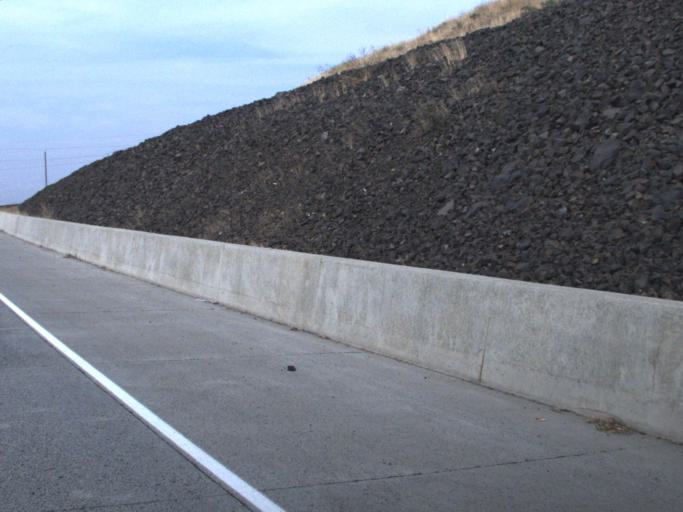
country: US
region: Washington
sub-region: Spokane County
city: Mead
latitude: 47.7391
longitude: -117.3606
